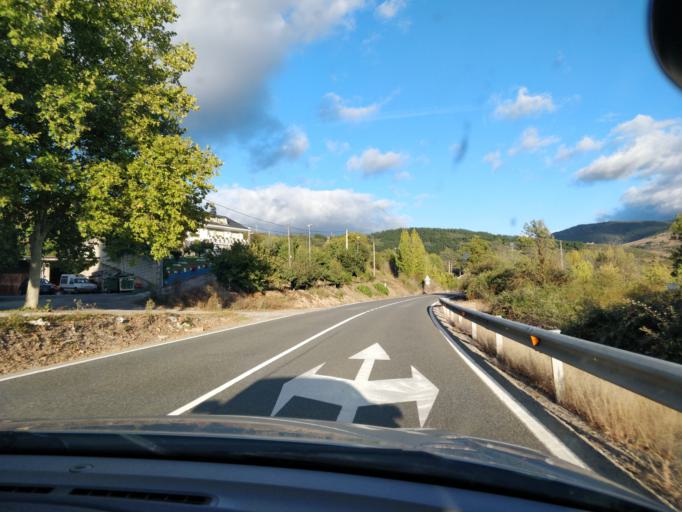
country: ES
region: Castille and Leon
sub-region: Provincia de Leon
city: Borrenes
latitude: 42.4998
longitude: -6.7284
